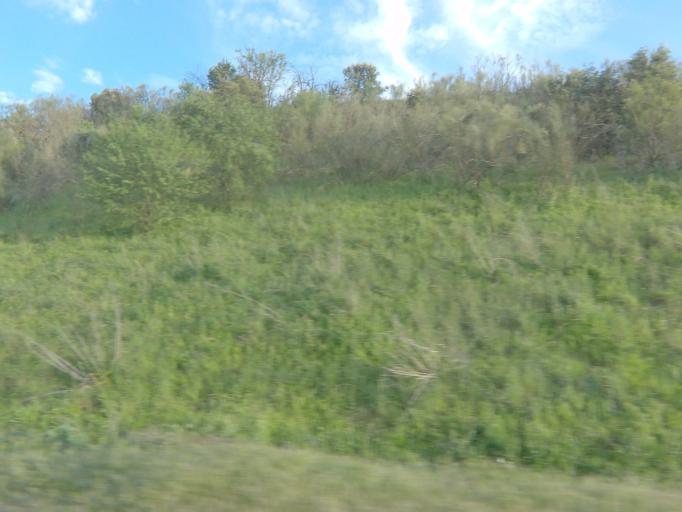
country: ES
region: Extremadura
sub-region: Provincia de Badajoz
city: Lobon
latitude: 38.8593
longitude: -6.5716
